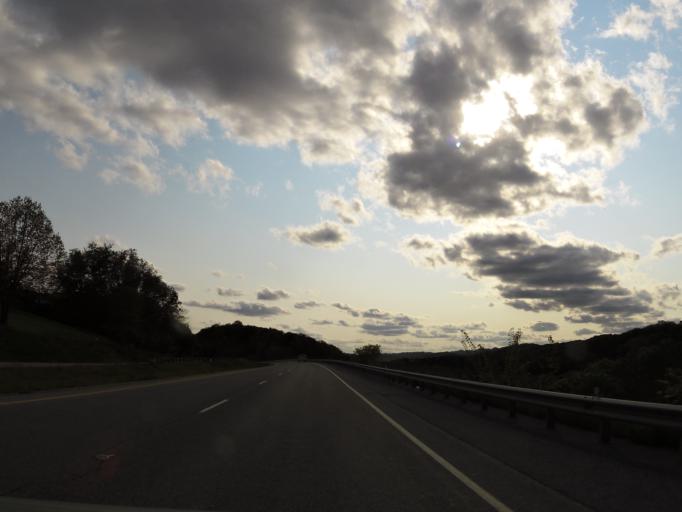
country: US
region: Virginia
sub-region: Tazewell County
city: Bluefield
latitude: 37.2381
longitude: -81.2790
